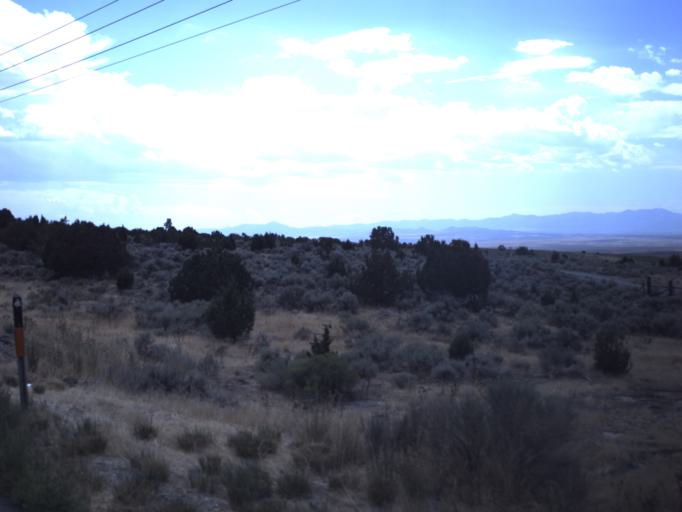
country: US
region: Utah
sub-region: Tooele County
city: Tooele
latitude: 40.3412
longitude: -112.3032
